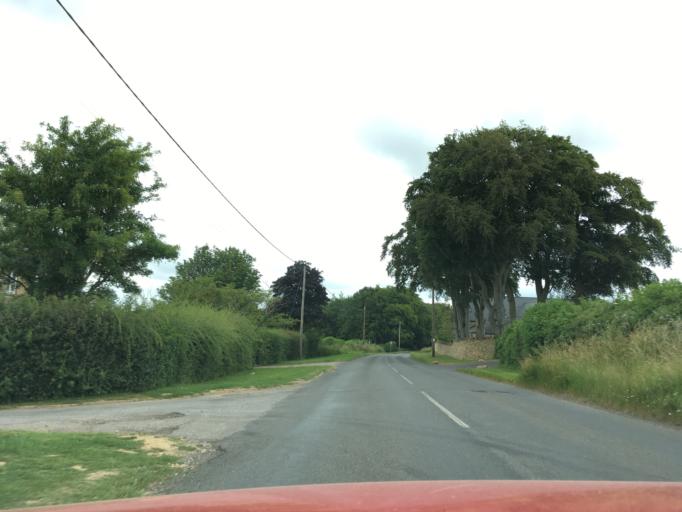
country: GB
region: England
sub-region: Oxfordshire
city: Chipping Norton
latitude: 51.9264
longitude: -1.5790
